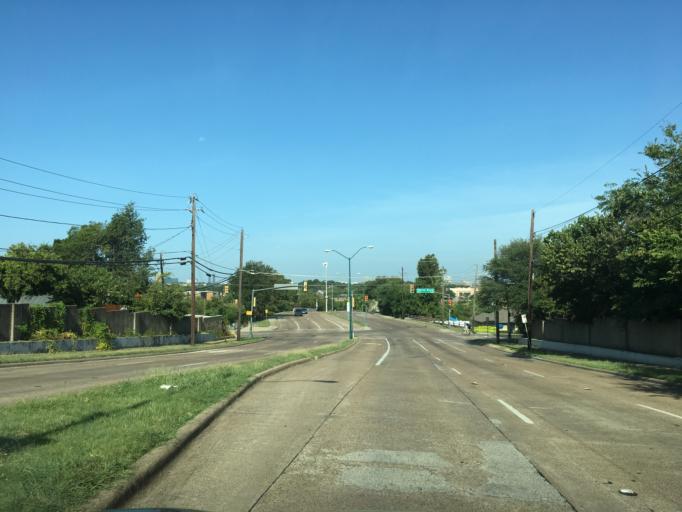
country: US
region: Texas
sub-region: Dallas County
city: Richardson
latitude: 32.8789
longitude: -96.7284
